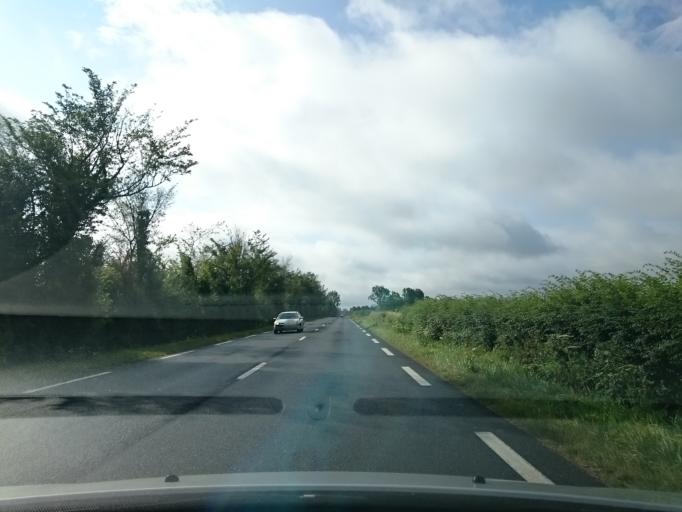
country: FR
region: Lower Normandy
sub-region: Departement du Calvados
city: Cambremer
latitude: 49.1314
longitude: 0.0008
